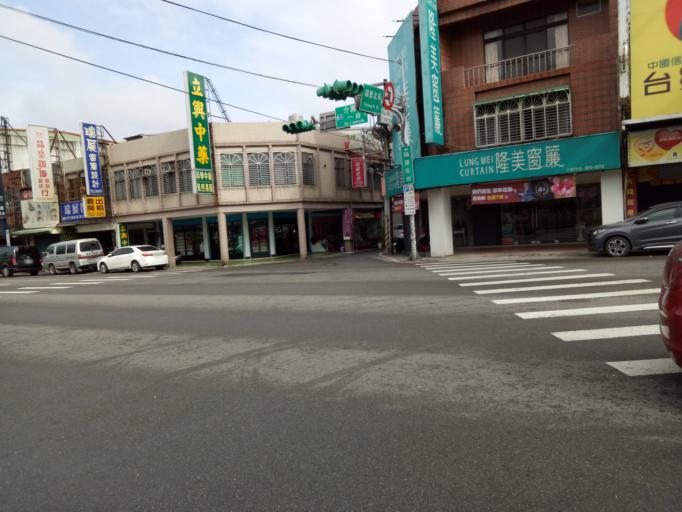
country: TW
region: Taiwan
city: Taoyuan City
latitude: 24.9650
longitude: 121.3005
